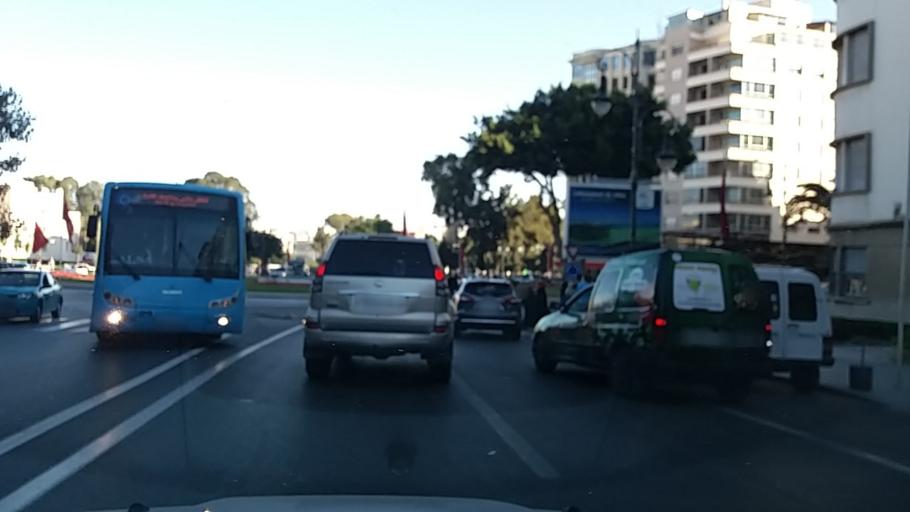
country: MA
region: Tanger-Tetouan
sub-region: Tanger-Assilah
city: Tangier
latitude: 35.7780
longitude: -5.8196
